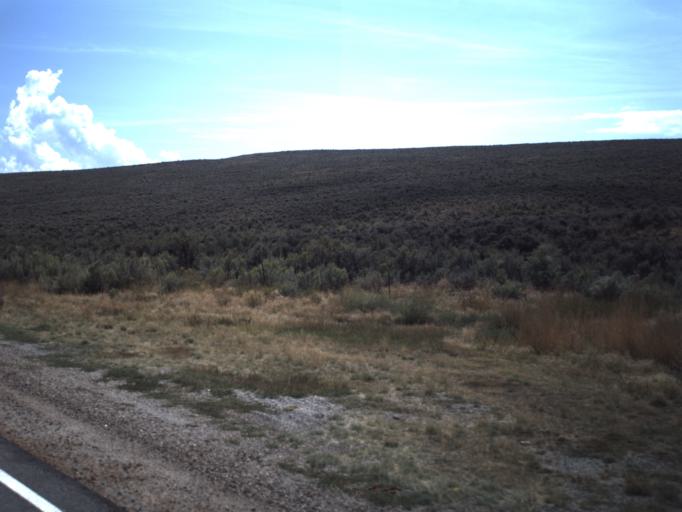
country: US
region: Utah
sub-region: Rich County
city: Randolph
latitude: 41.7789
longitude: -111.1954
